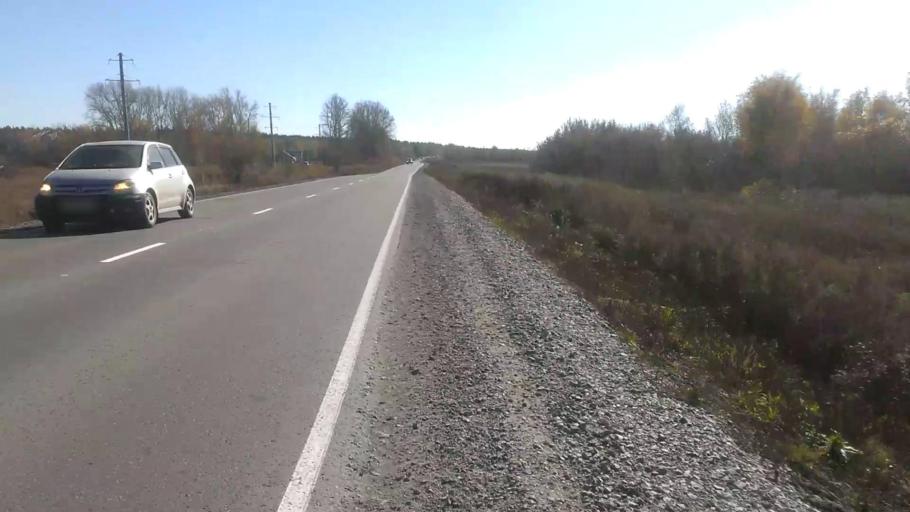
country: RU
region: Altai Krai
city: Sannikovo
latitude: 53.3098
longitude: 83.9667
